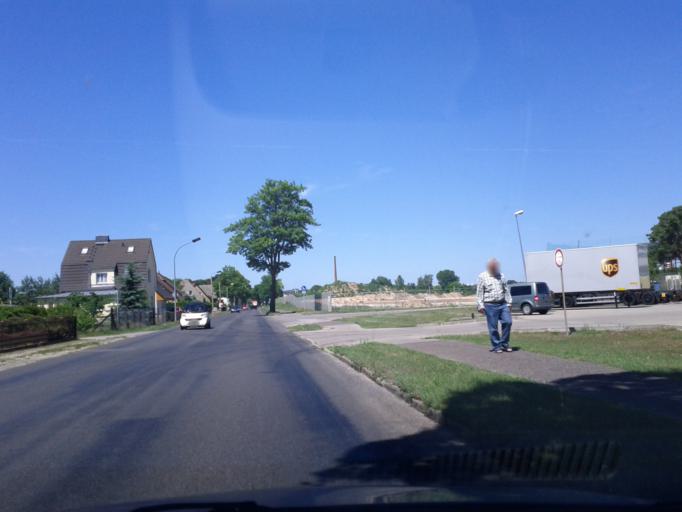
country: DE
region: Brandenburg
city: Langewahl
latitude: 52.3460
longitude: 14.0805
